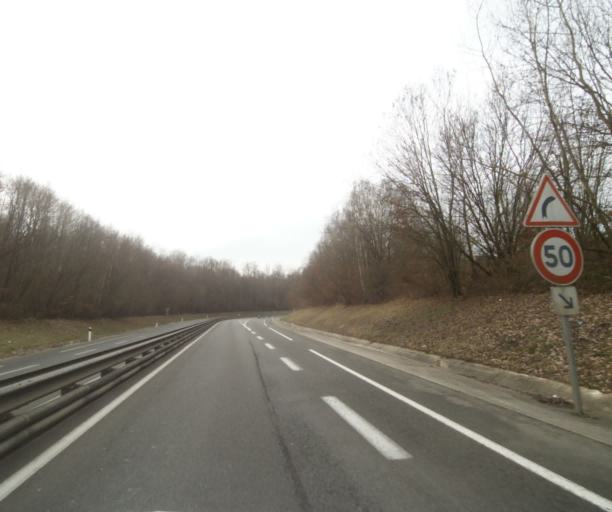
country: FR
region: Champagne-Ardenne
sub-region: Departement de la Haute-Marne
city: Bettancourt-la-Ferree
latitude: 48.6207
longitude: 4.9875
